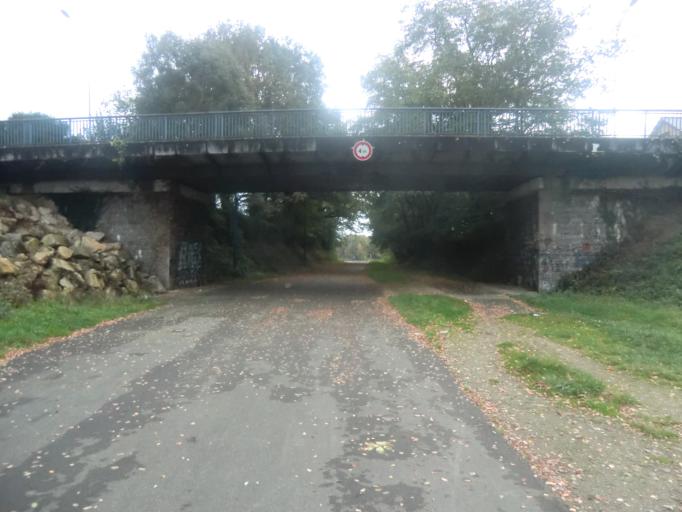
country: FR
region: Pays de la Loire
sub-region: Departement de la Mayenne
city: Mayenne
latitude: 48.2955
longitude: -0.6132
